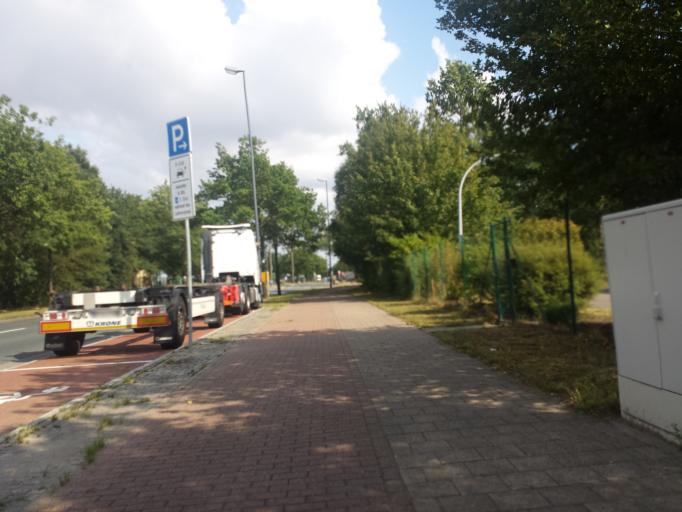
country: DE
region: Lower Saxony
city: Stuhr
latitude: 53.0861
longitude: 8.7159
